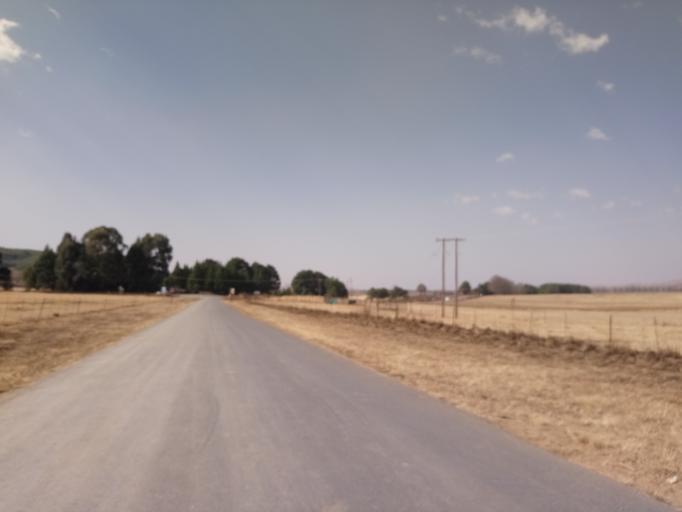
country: ZA
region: KwaZulu-Natal
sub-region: uMgungundlovu District Municipality
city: Mooirivier
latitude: -29.3225
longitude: 29.7185
